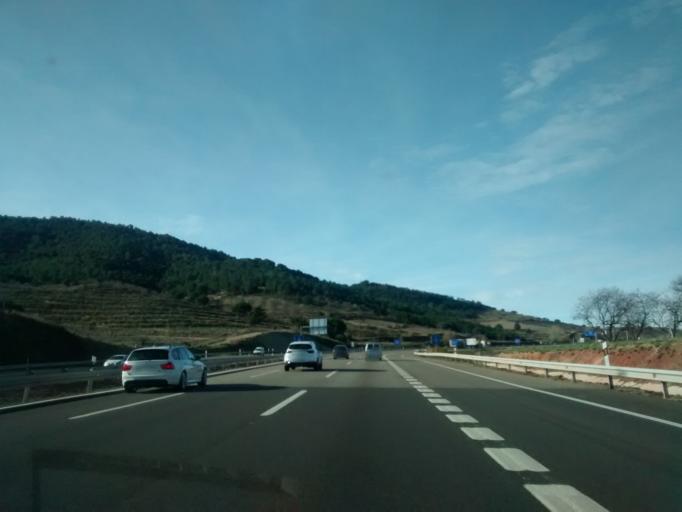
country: ES
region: Aragon
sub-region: Provincia de Zaragoza
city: Paracuellos de la Ribera
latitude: 41.4128
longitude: -1.5081
